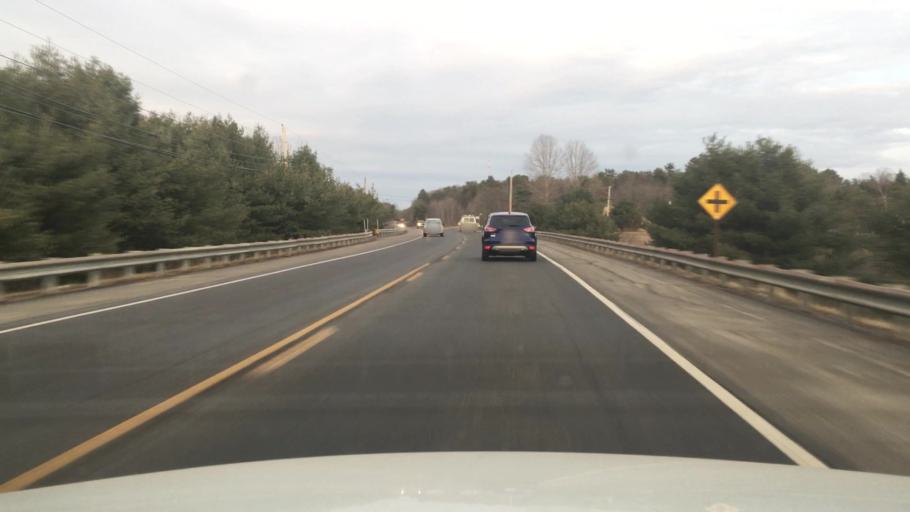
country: US
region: Maine
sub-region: Lincoln County
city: Damariscotta
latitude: 44.0149
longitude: -69.5848
